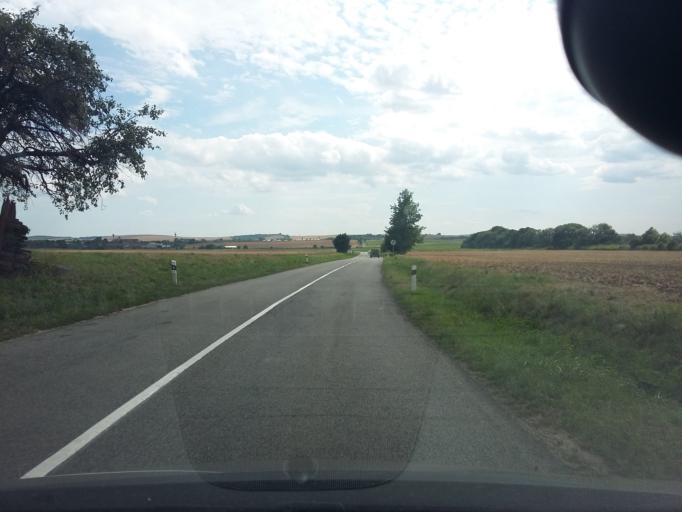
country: SK
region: Trnavsky
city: Gbely
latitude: 48.7432
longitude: 17.1707
